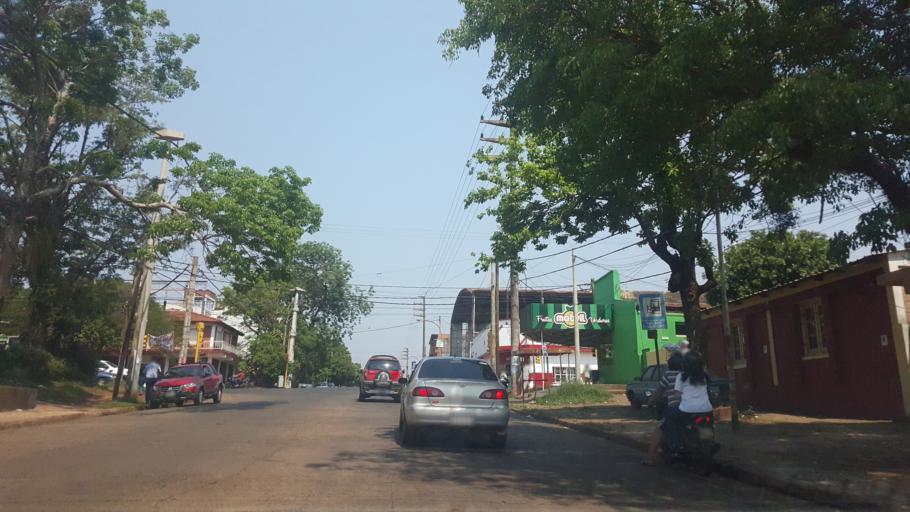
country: AR
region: Misiones
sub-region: Departamento de Capital
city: Posadas
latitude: -27.3726
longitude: -55.9097
